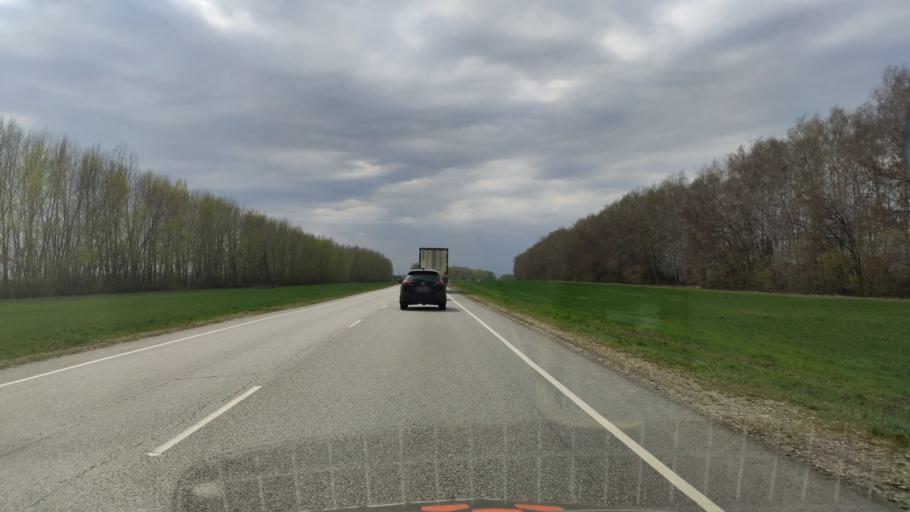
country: RU
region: Kursk
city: Olym
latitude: 51.5522
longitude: 38.2143
